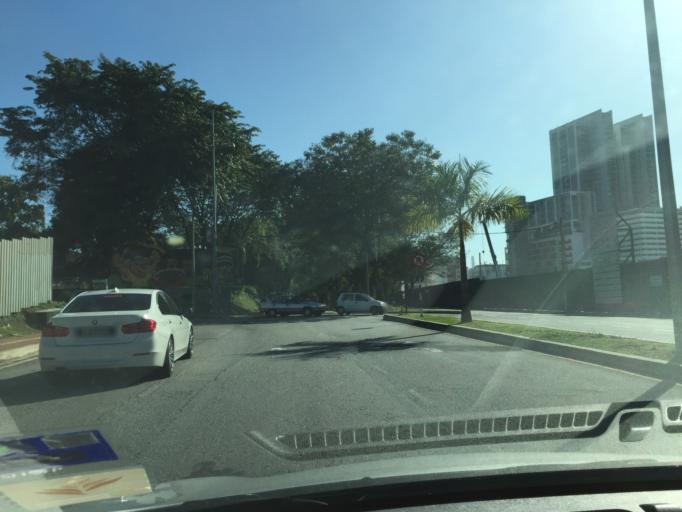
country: MY
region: Selangor
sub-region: Petaling
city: Petaling Jaya
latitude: 3.1184
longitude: 101.6313
